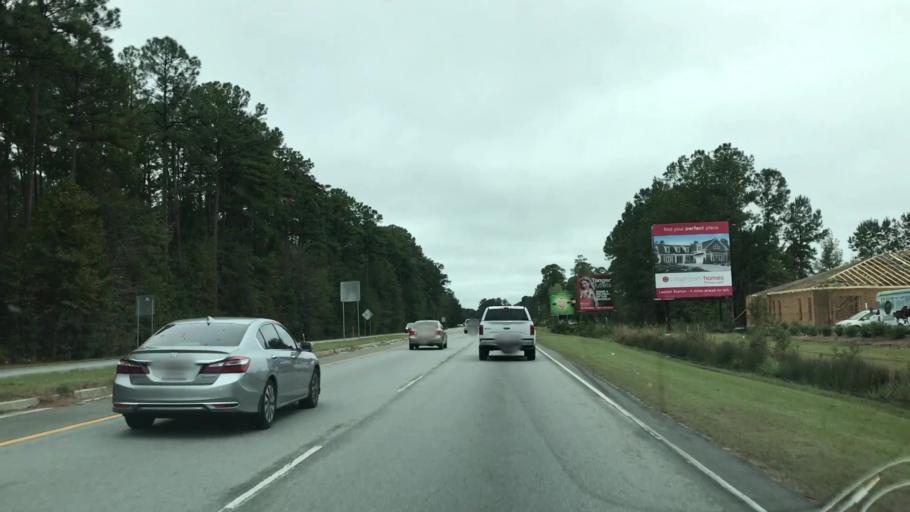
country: US
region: South Carolina
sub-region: Beaufort County
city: Bluffton
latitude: 32.3082
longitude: -80.9351
